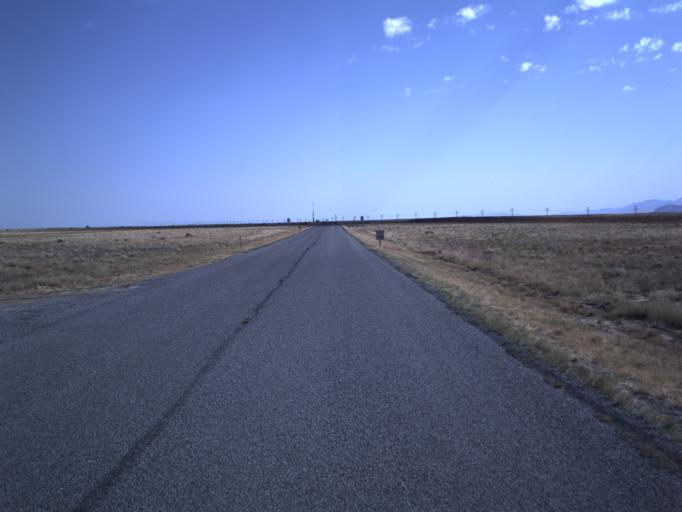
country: US
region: Utah
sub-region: Millard County
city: Fillmore
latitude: 38.9132
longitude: -112.8153
